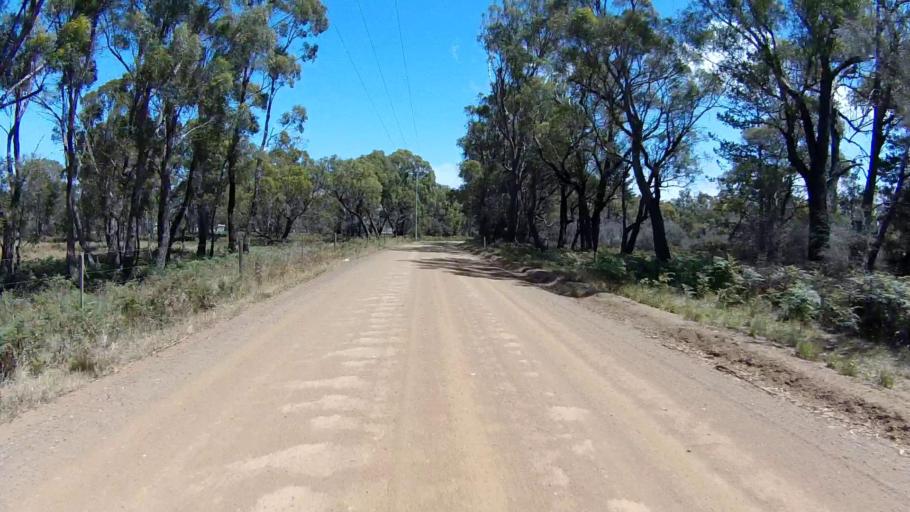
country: AU
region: Tasmania
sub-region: Clarence
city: Sandford
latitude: -42.9336
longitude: 147.5131
